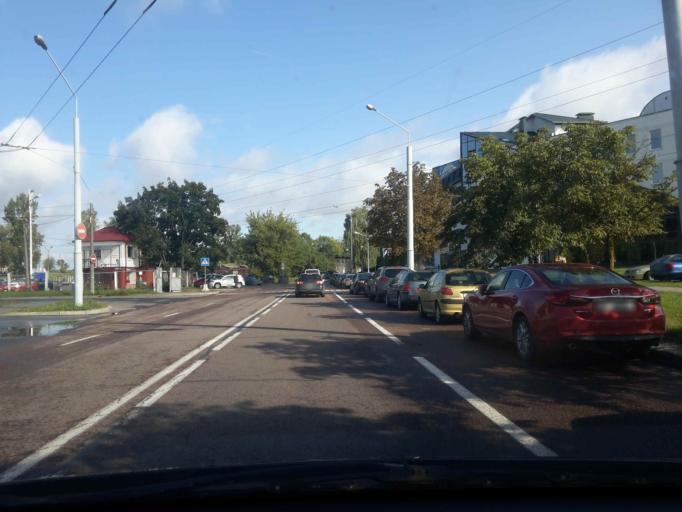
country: BY
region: Minsk
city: Minsk
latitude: 53.9410
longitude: 27.5661
